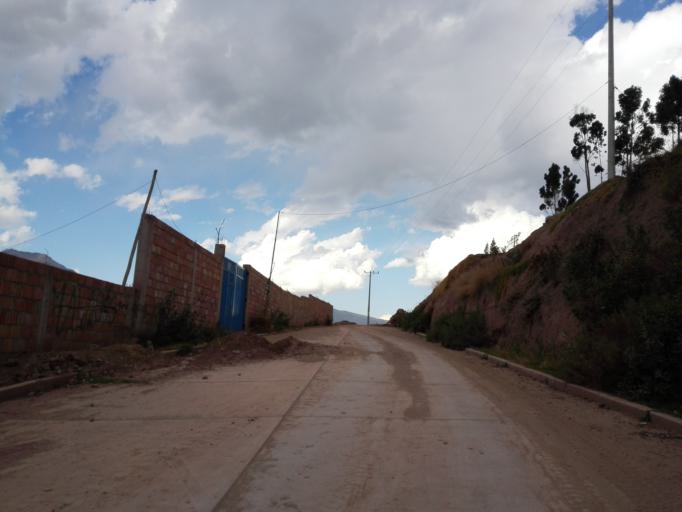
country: PE
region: Cusco
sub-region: Provincia de Cusco
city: Cusco
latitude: -13.5399
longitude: -71.9473
